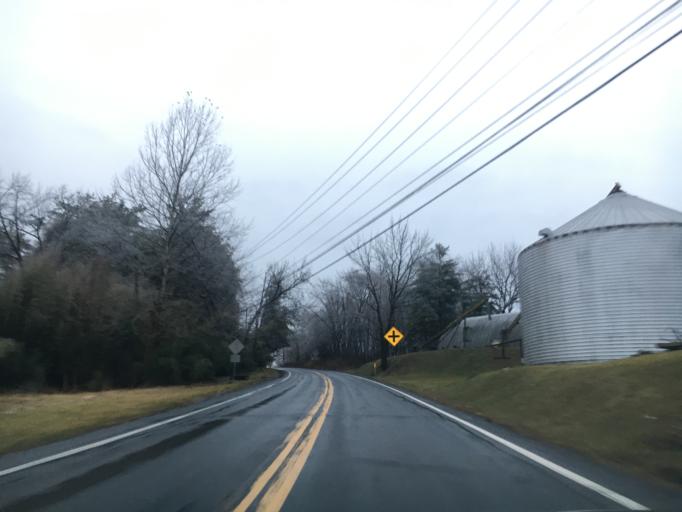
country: US
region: Pennsylvania
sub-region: Lehigh County
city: Schnecksville
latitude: 40.6330
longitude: -75.6012
